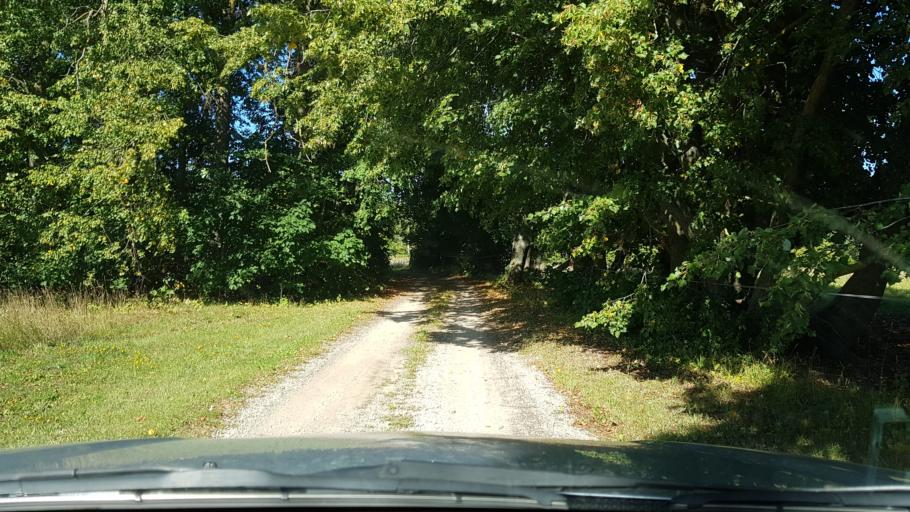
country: EE
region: Ida-Virumaa
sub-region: Sillamaee linn
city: Sillamae
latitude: 59.3936
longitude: 27.8465
